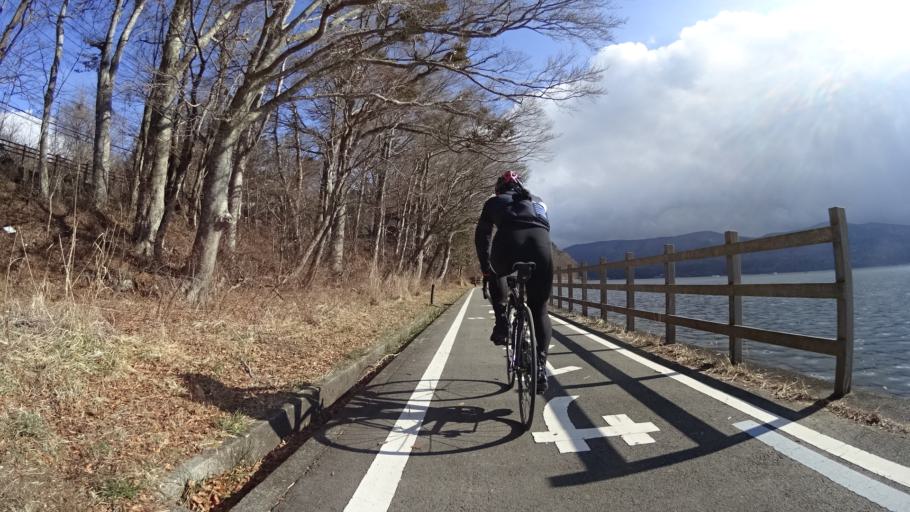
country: JP
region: Shizuoka
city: Gotemba
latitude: 35.4249
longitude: 138.8781
